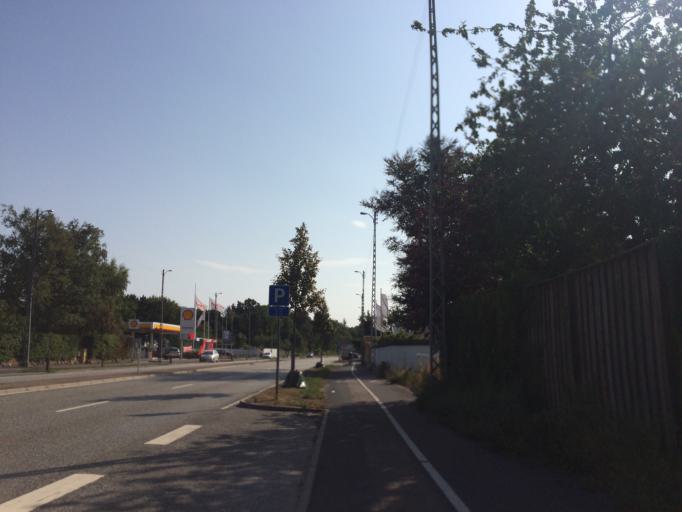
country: DK
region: Capital Region
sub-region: Ishoj Kommune
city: Ishoj
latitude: 55.5995
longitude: 12.3489
